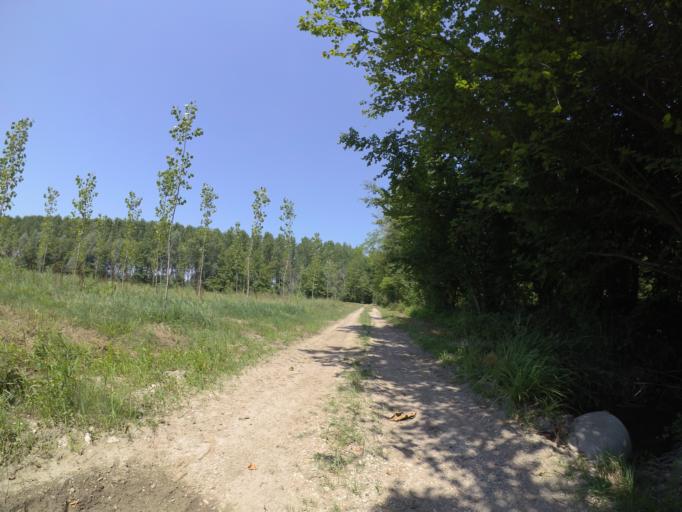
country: IT
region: Friuli Venezia Giulia
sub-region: Provincia di Udine
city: Rivignano
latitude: 45.8970
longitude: 13.0396
